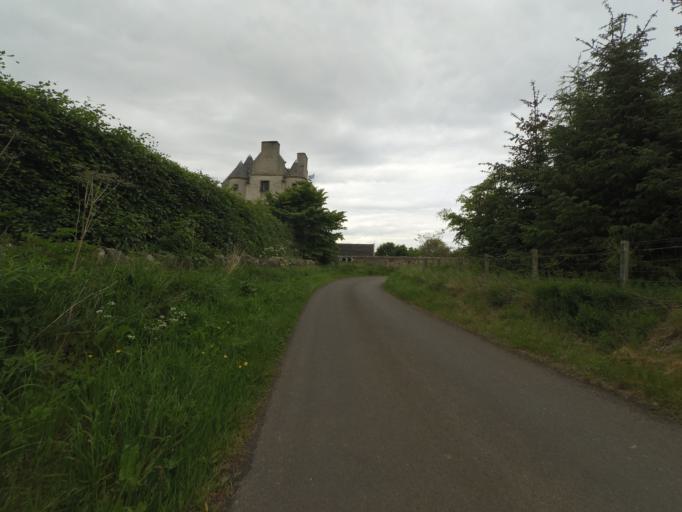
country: GB
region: Scotland
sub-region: East Lothian
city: Prestonpans
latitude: 55.9276
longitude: -2.9967
